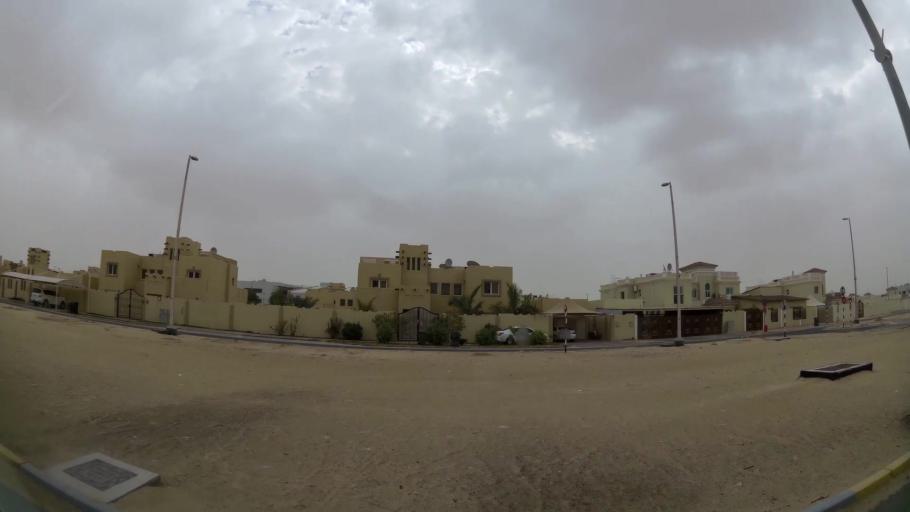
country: AE
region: Abu Dhabi
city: Abu Dhabi
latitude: 24.4458
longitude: 54.7177
